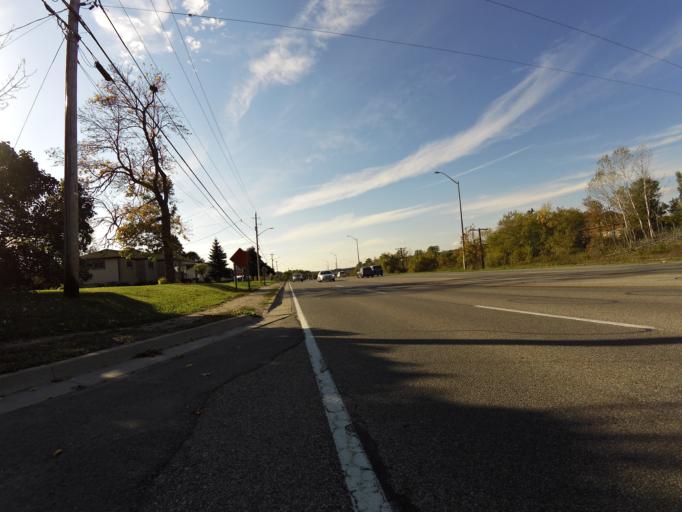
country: CA
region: Ontario
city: Kingston
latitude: 44.2373
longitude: -76.5863
